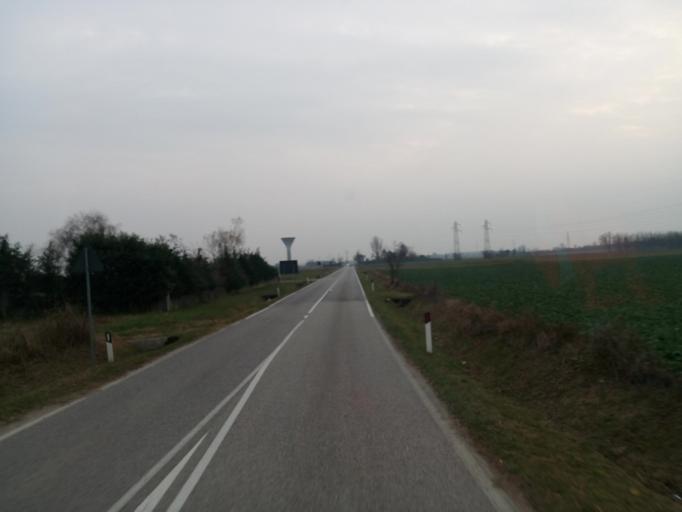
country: IT
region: Friuli Venezia Giulia
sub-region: Provincia di Udine
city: Reana del Rojale
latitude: 46.1181
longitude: 13.2514
